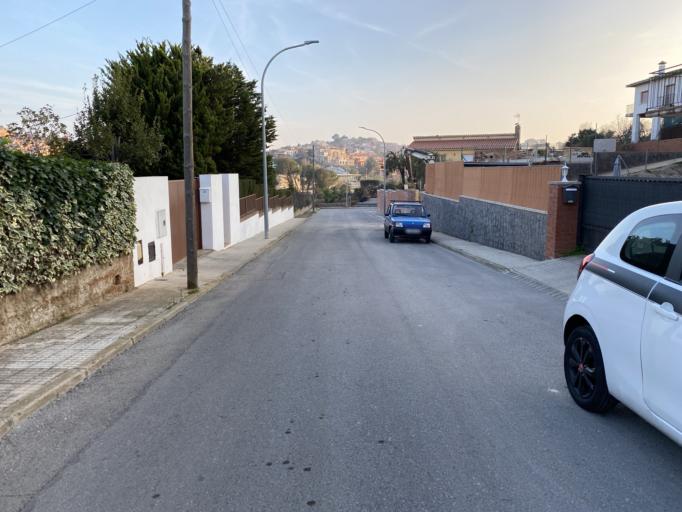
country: ES
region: Catalonia
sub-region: Provincia de Barcelona
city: Viladecavalls
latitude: 41.5591
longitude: 1.9521
